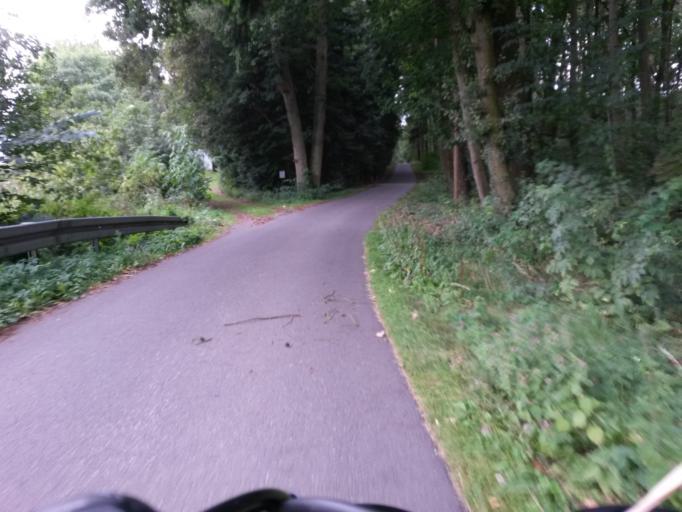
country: DE
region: Brandenburg
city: Angermunde
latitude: 53.0521
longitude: 13.9422
